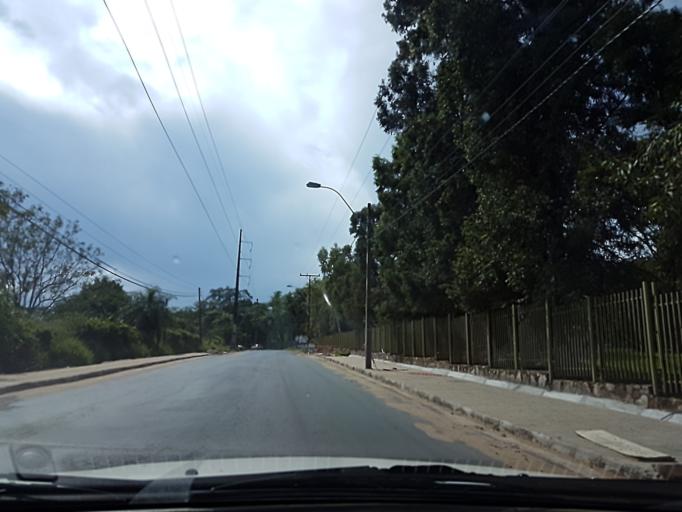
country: PY
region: Asuncion
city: Asuncion
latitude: -25.2474
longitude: -57.5783
